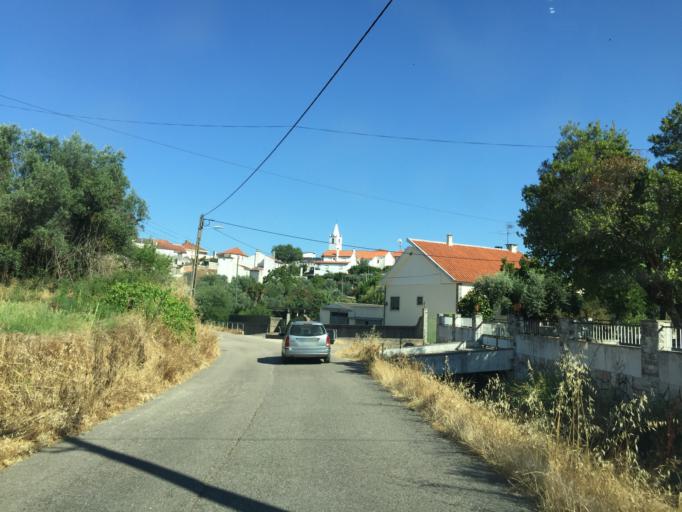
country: PT
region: Santarem
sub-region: Tomar
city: Tomar
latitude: 39.6076
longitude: -8.3314
